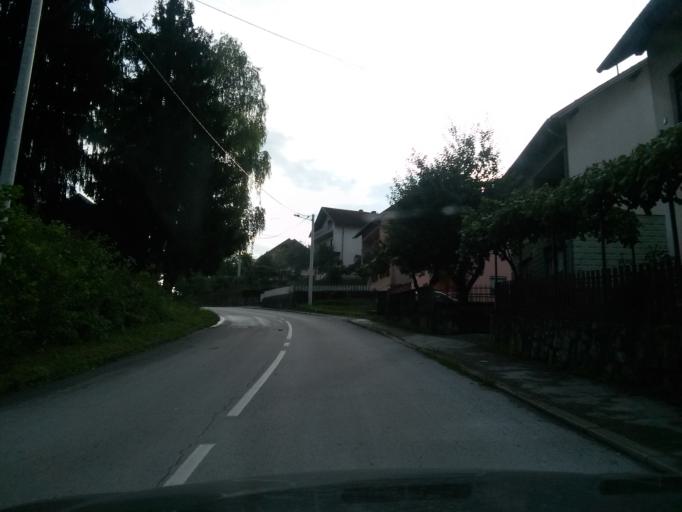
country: HR
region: Sisacko-Moslavacka
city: Gvozd
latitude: 45.2929
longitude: 15.9654
